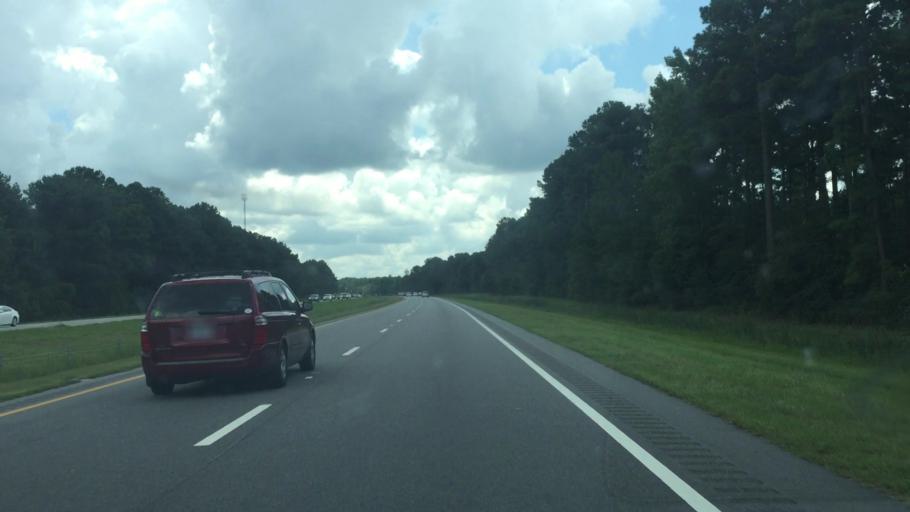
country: US
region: North Carolina
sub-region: Columbus County
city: Chadbourn
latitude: 34.4174
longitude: -78.9375
